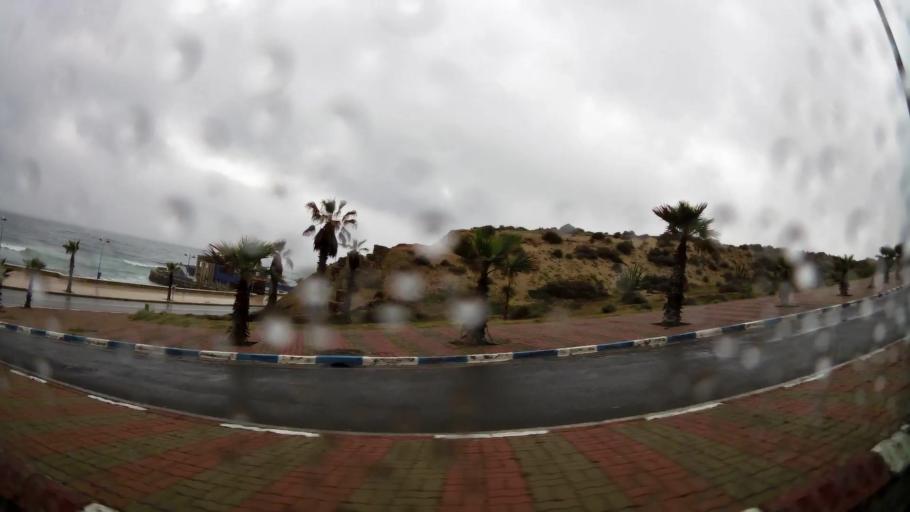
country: MA
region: Taza-Al Hoceima-Taounate
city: Tirhanimine
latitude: 35.2467
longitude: -3.9580
